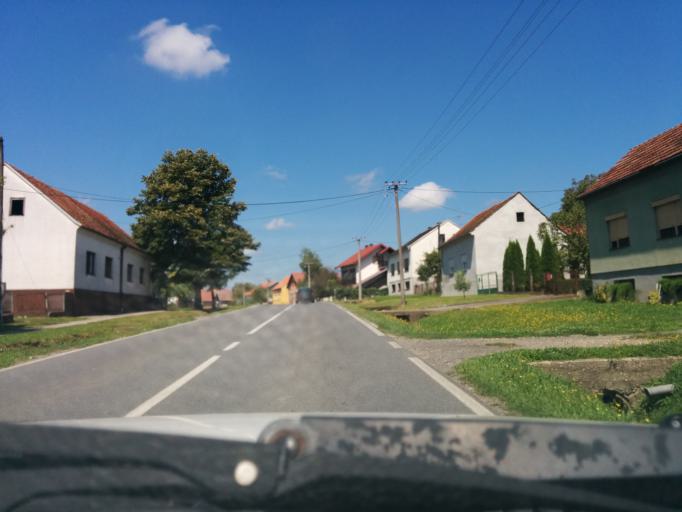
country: HR
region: Sisacko-Moslavacka
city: Novska
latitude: 45.3607
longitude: 16.9514
